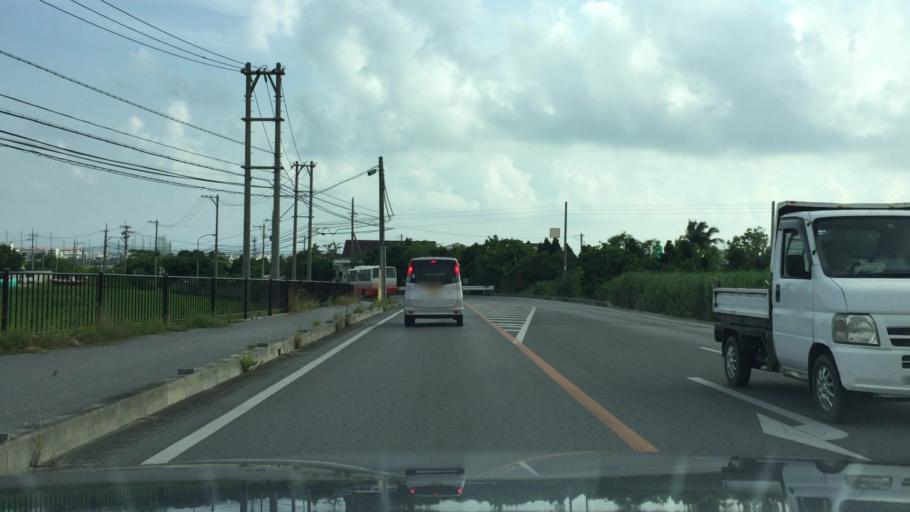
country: JP
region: Okinawa
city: Ishigaki
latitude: 24.3521
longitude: 124.1732
